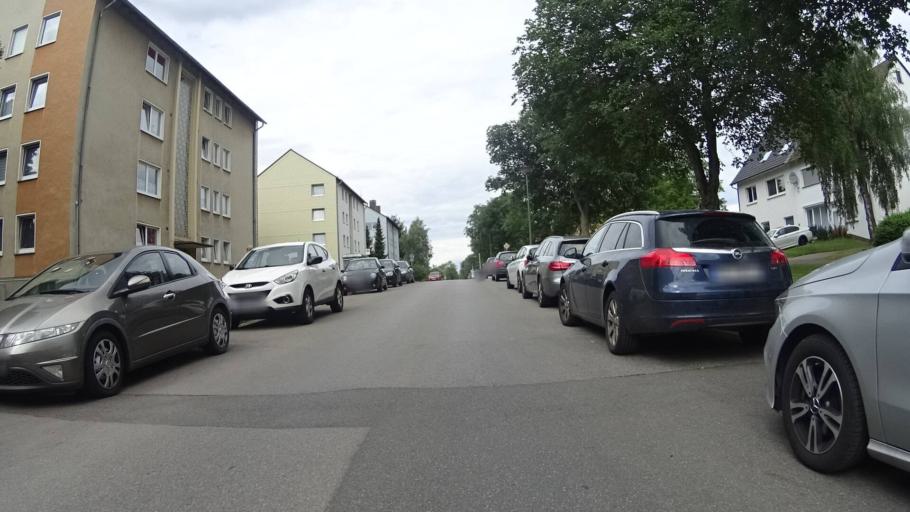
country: DE
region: Lower Saxony
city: Holzminden
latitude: 51.8198
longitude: 9.4642
